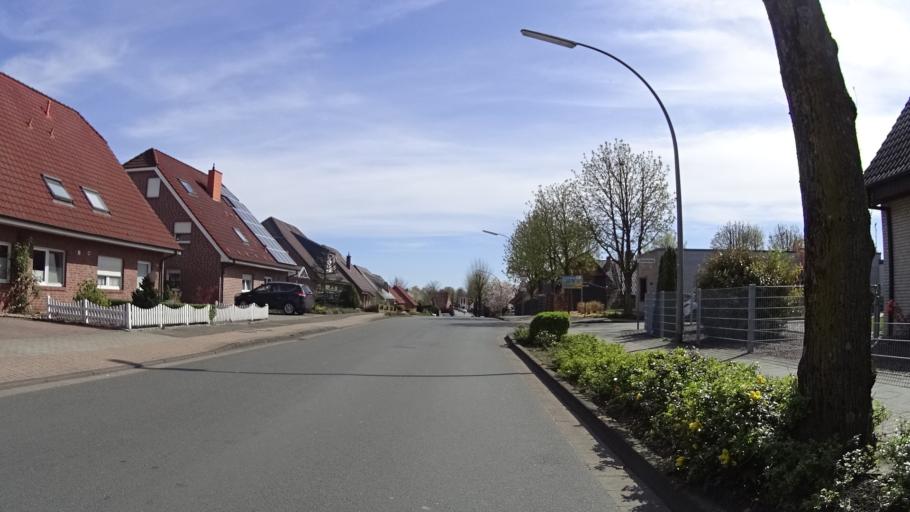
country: DE
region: North Rhine-Westphalia
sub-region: Regierungsbezirk Munster
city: Dreierwalde
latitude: 52.2919
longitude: 7.4715
